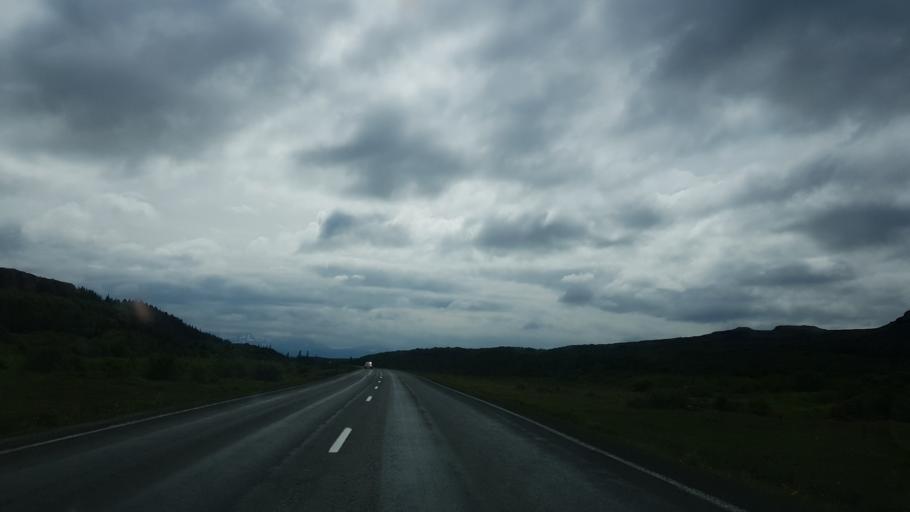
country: IS
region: West
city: Borgarnes
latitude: 64.7315
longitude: -21.5950
